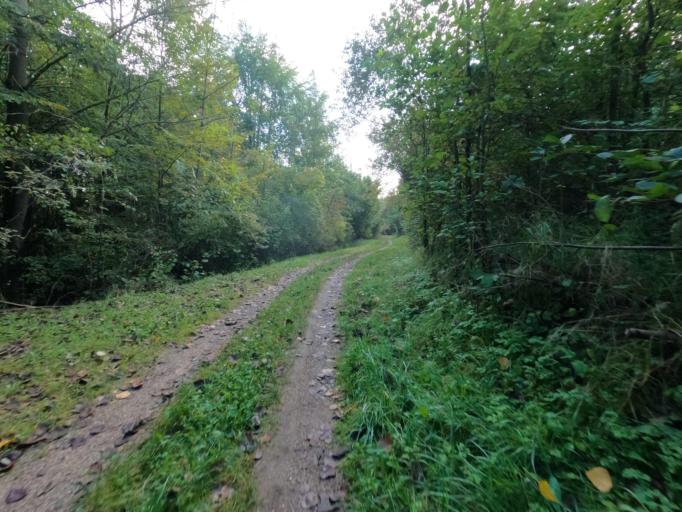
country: DE
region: North Rhine-Westphalia
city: Neu-Pattern
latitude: 50.8614
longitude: 6.3149
